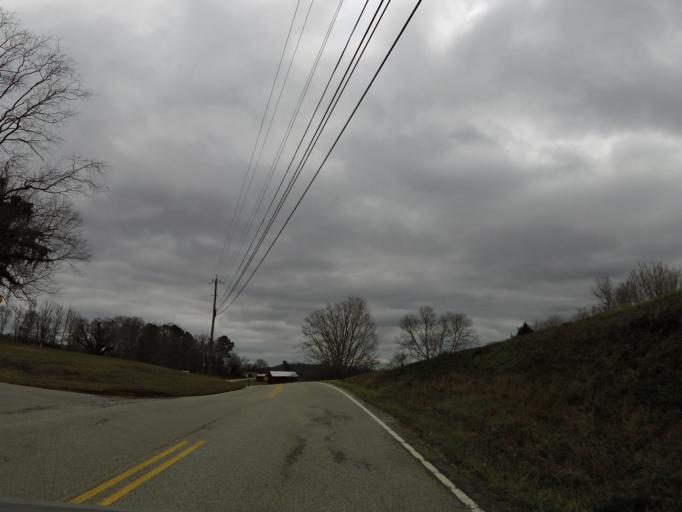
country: US
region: Tennessee
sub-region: Grainger County
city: Blaine
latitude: 36.1447
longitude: -83.6516
